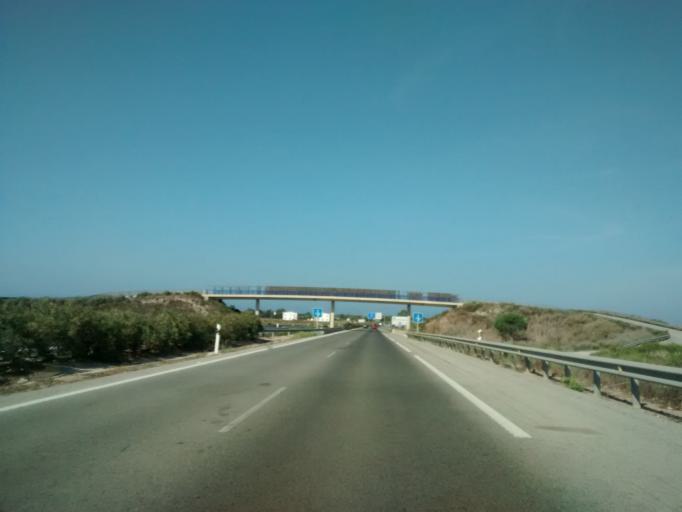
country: ES
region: Andalusia
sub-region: Provincia de Cadiz
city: Conil de la Frontera
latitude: 36.3557
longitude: -6.0933
